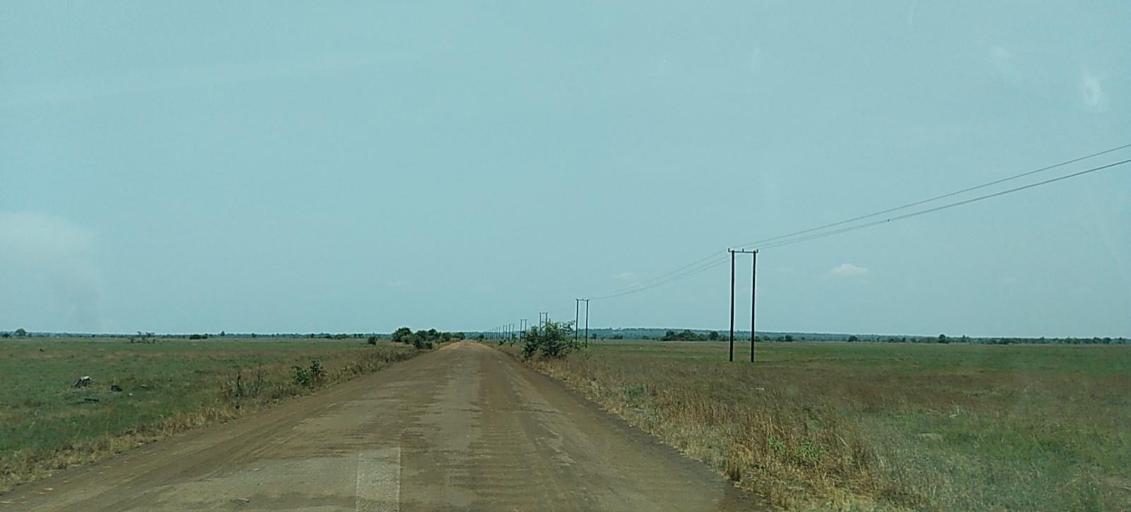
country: ZM
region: Copperbelt
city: Mpongwe
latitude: -13.6622
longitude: 27.8511
